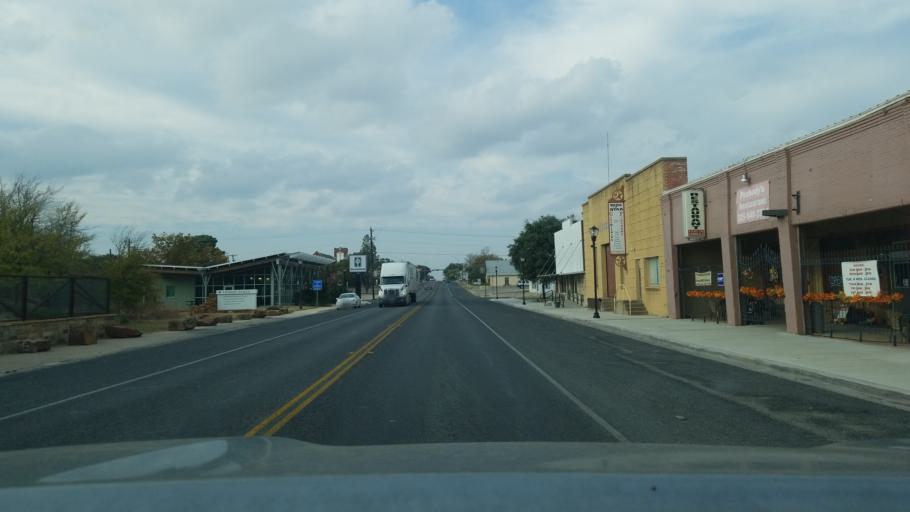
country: US
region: Texas
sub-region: Mills County
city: Goldthwaite
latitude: 31.4516
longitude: -98.5697
